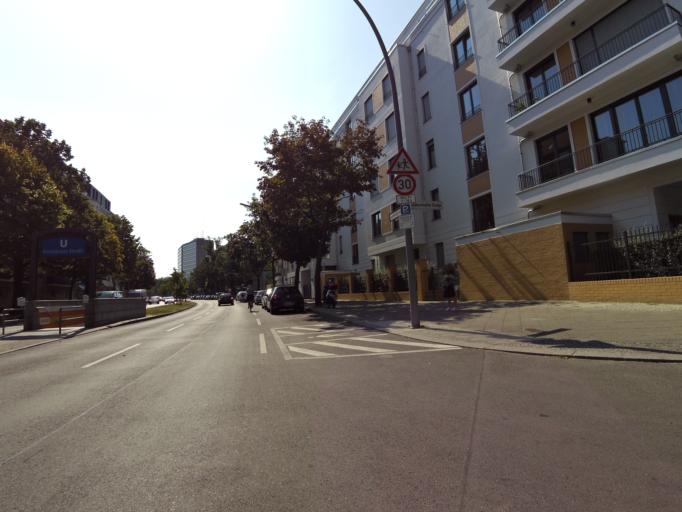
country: DE
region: Berlin
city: Halensee
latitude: 52.4953
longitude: 13.3084
